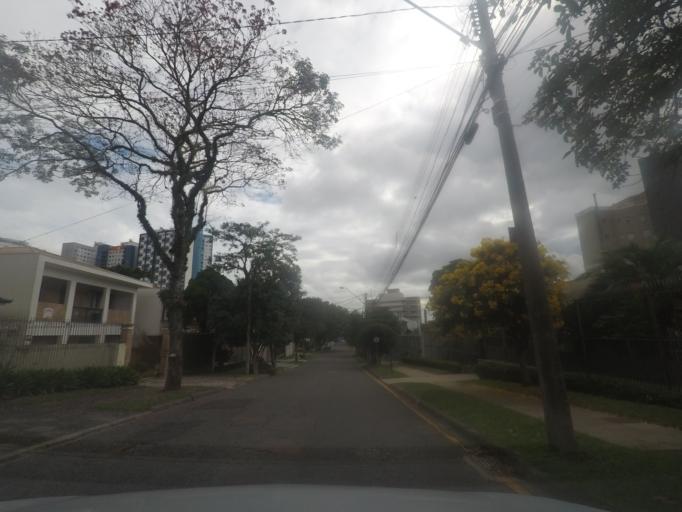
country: BR
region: Parana
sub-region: Curitiba
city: Curitiba
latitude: -25.4338
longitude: -49.2403
